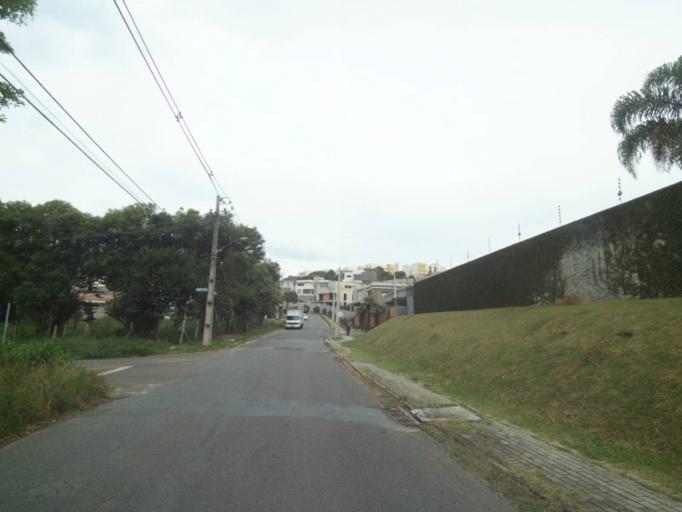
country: BR
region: Parana
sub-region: Curitiba
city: Curitiba
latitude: -25.4058
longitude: -49.2973
